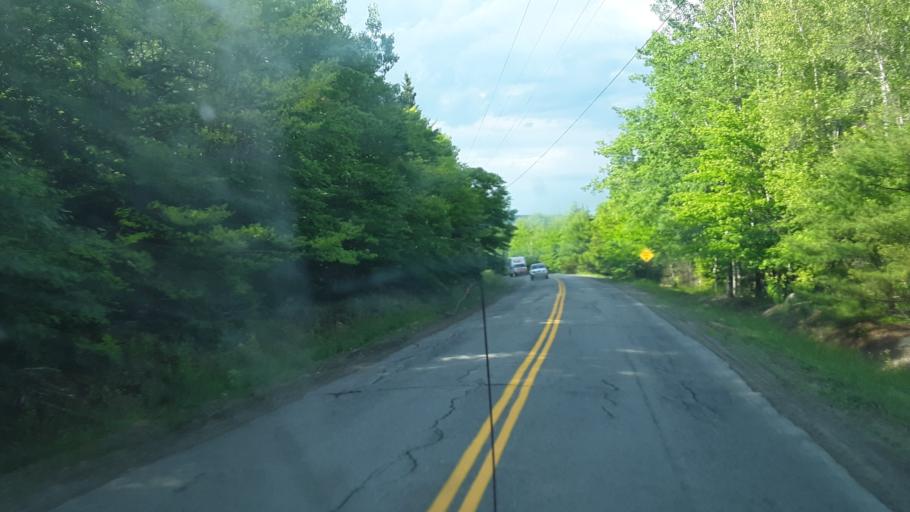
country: US
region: Maine
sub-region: Washington County
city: Calais
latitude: 45.1056
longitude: -67.5087
